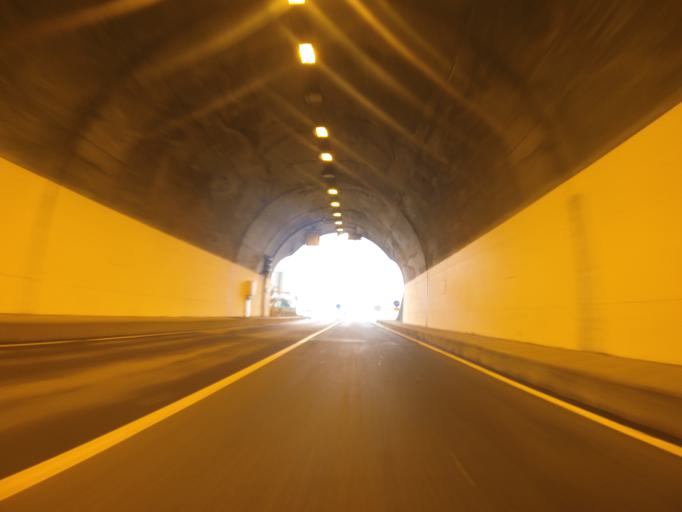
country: PT
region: Madeira
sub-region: Camara de Lobos
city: Curral das Freiras
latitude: 32.7050
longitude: -16.9540
